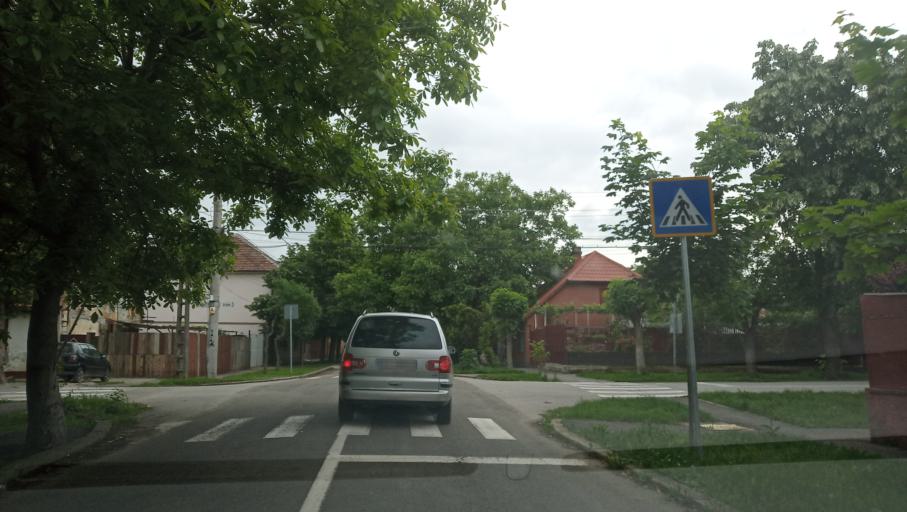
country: RO
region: Timis
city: Timisoara
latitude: 45.7486
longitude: 21.2607
